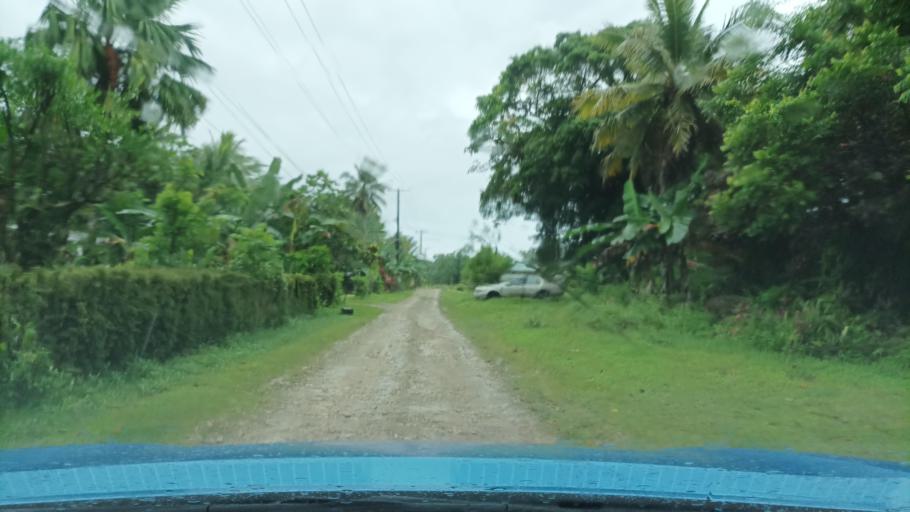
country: FM
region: Pohnpei
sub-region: Kolonia Municipality
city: Kolonia
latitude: 6.9569
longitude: 158.2142
